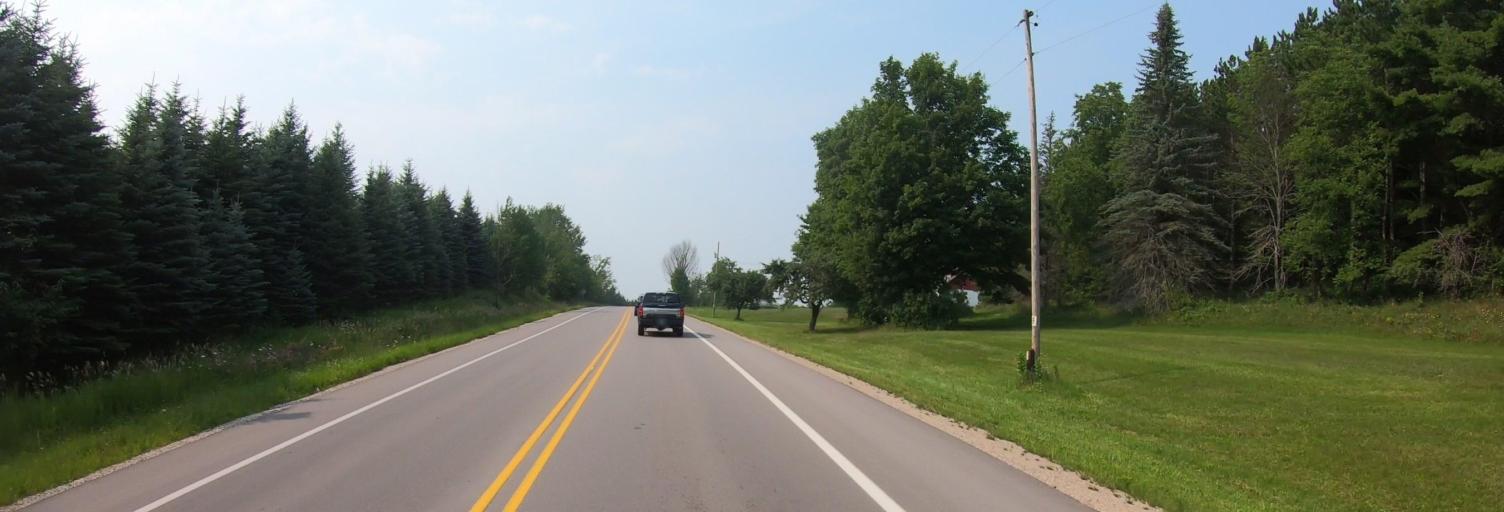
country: US
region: Michigan
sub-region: Charlevoix County
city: Charlevoix
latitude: 45.2564
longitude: -85.2620
